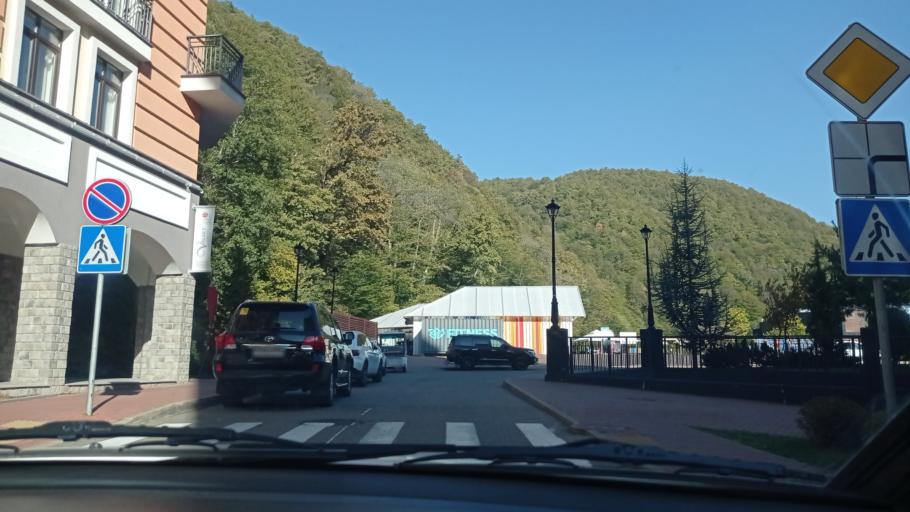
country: RU
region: Krasnodarskiy
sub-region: Sochi City
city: Krasnaya Polyana
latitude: 43.6733
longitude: 40.2977
